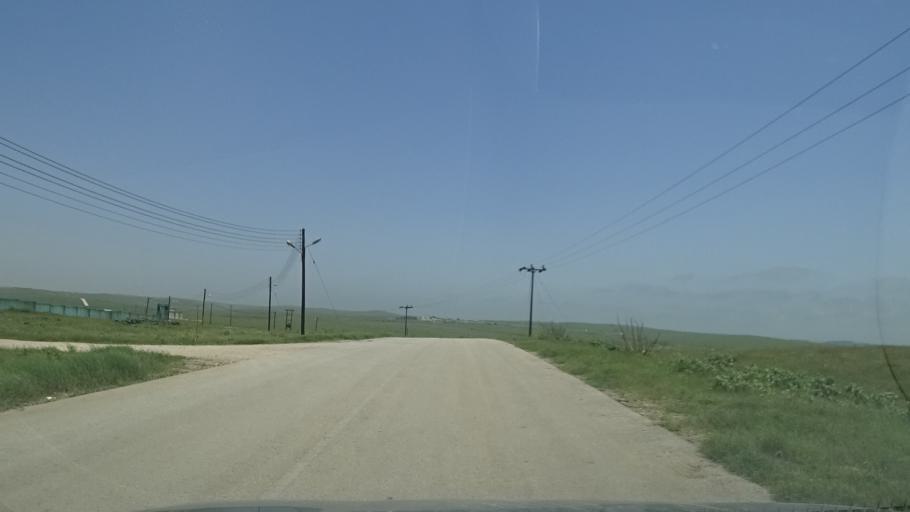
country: OM
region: Zufar
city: Salalah
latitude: 17.2488
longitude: 54.2654
